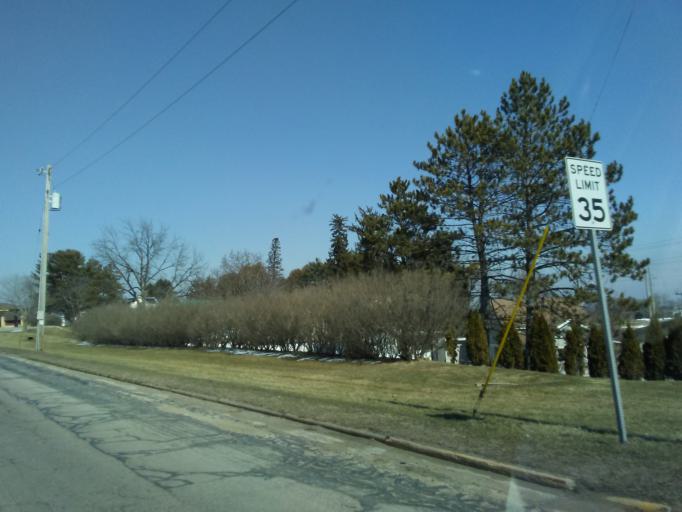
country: US
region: Wisconsin
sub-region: Vernon County
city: Westby
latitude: 43.6567
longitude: -90.8558
